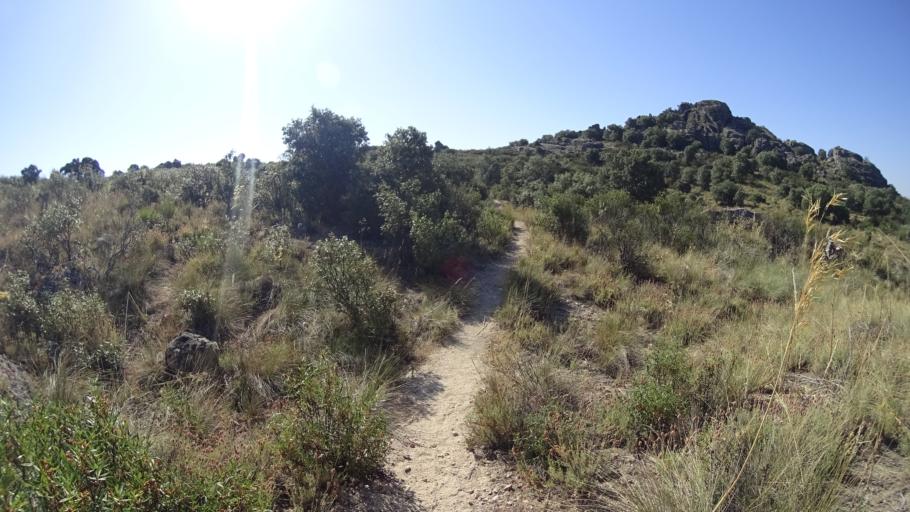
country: ES
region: Madrid
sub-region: Provincia de Madrid
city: Hoyo de Manzanares
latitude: 40.6477
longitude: -3.9379
